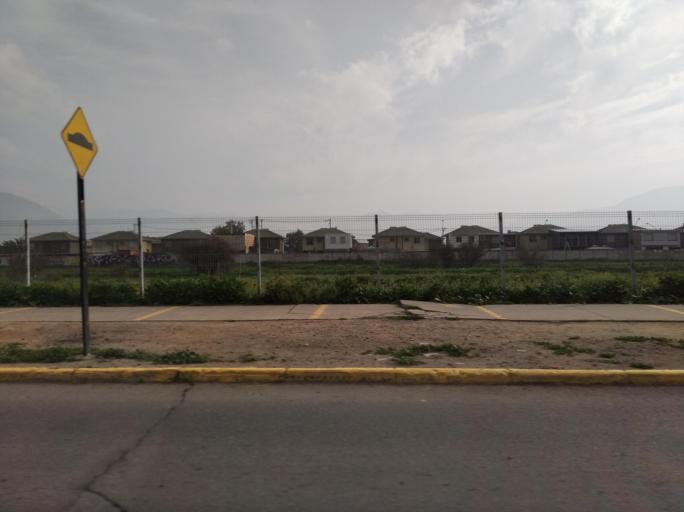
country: CL
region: Santiago Metropolitan
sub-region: Provincia de Chacabuco
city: Lampa
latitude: -33.2951
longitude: -70.8726
